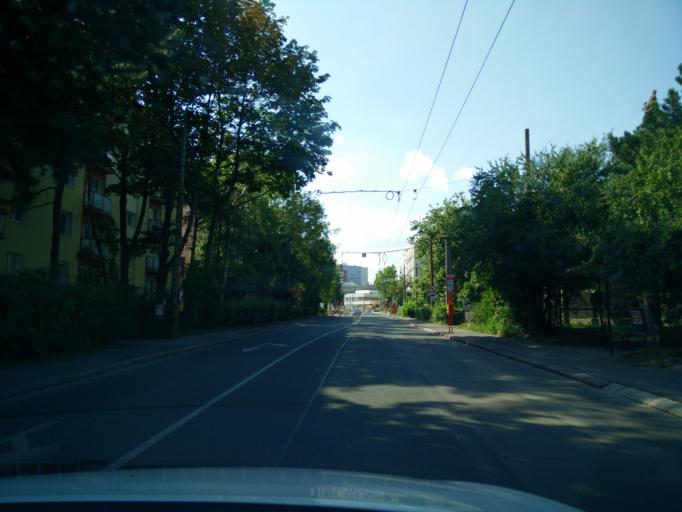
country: SK
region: Bratislavsky
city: Bratislava
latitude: 48.1658
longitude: 17.0947
